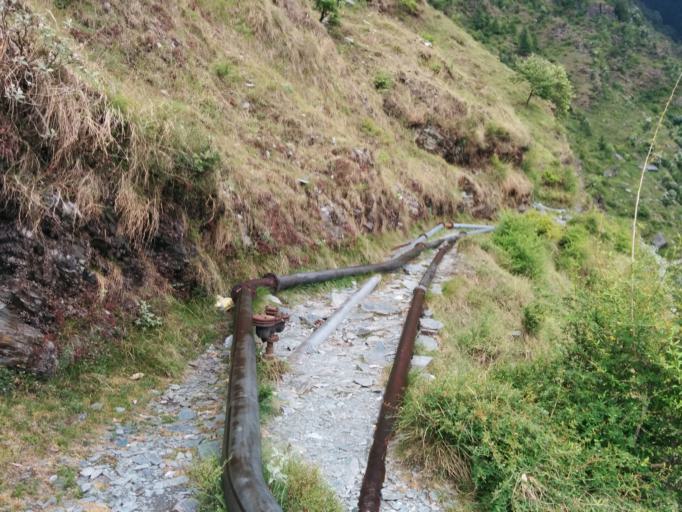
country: IN
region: Himachal Pradesh
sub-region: Kangra
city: Dharmsala
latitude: 32.2467
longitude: 76.3363
